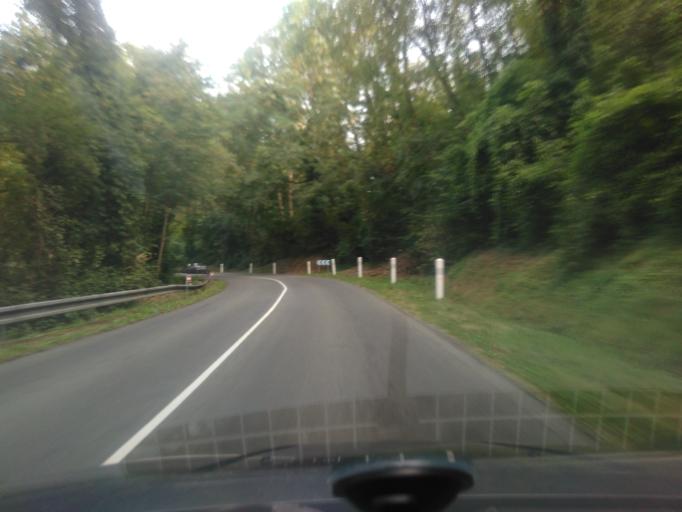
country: FR
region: Picardie
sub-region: Departement de l'Aisne
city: Bruyeres-et-Montberault
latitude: 49.5139
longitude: 3.6709
